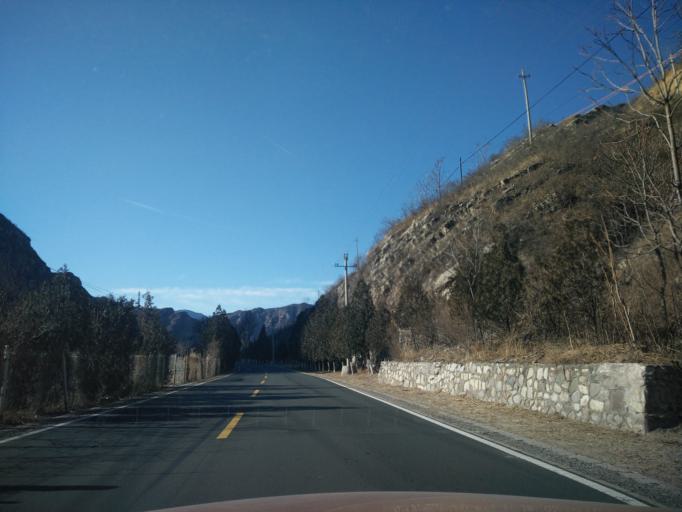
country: CN
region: Beijing
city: Yanchi
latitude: 40.0305
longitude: 115.8417
